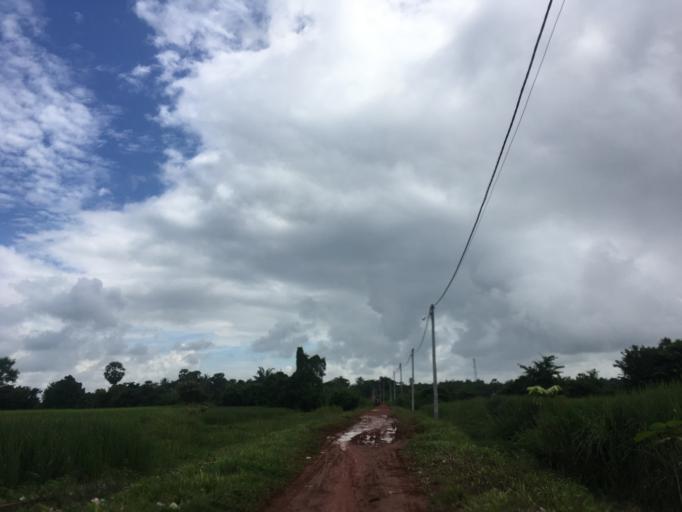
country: MM
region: Mon
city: Mawlamyine
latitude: 16.4649
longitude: 97.6837
